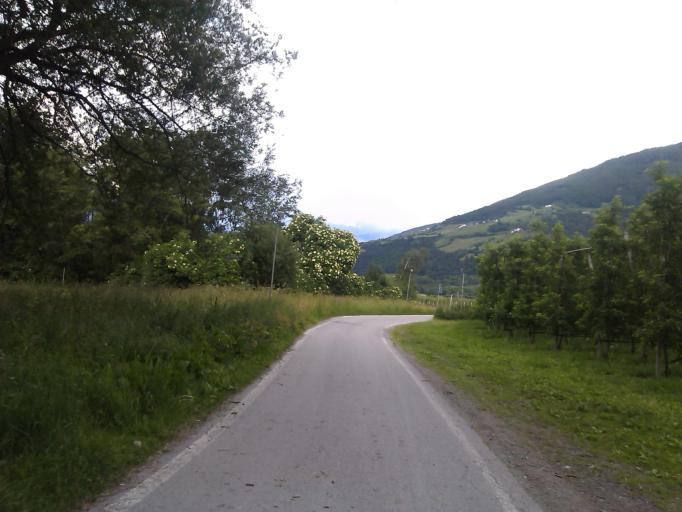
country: IT
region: Trentino-Alto Adige
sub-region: Bolzano
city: Prato Allo Stelvio
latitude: 46.6172
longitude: 10.6394
